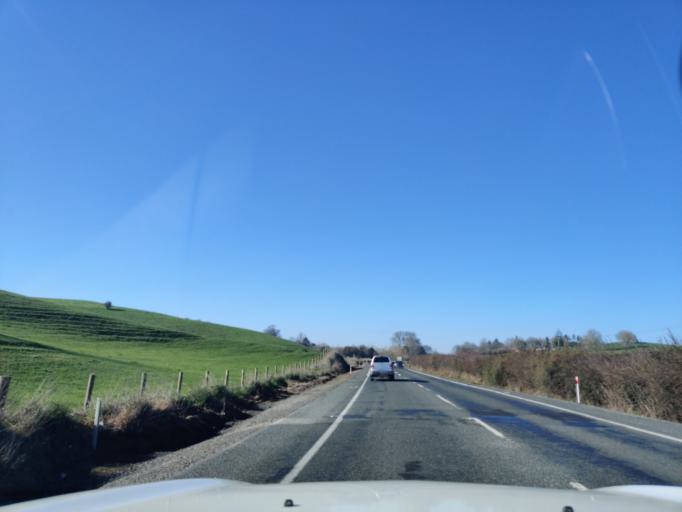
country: NZ
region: Waikato
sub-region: Matamata-Piako District
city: Matamata
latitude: -38.0065
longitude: 175.7700
